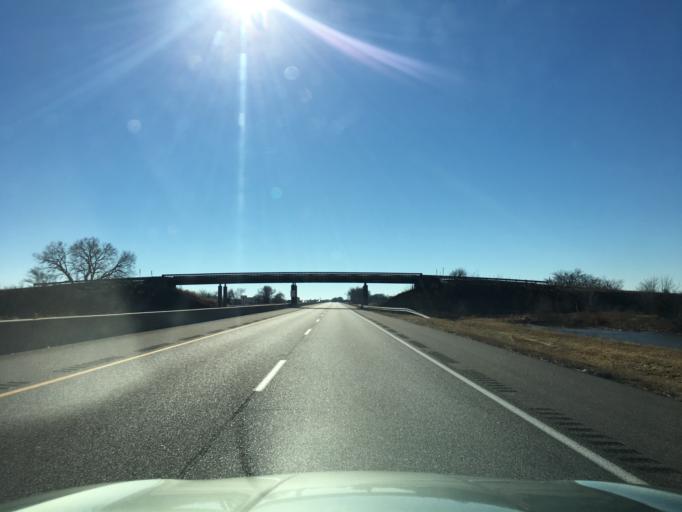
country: US
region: Kansas
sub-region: Sumner County
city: Mulvane
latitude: 37.4659
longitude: -97.3227
